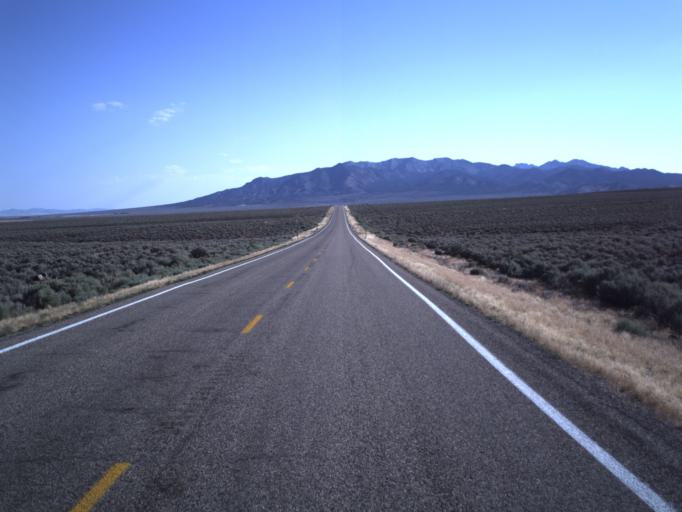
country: US
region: Utah
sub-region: Beaver County
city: Milford
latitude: 38.1541
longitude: -112.9585
